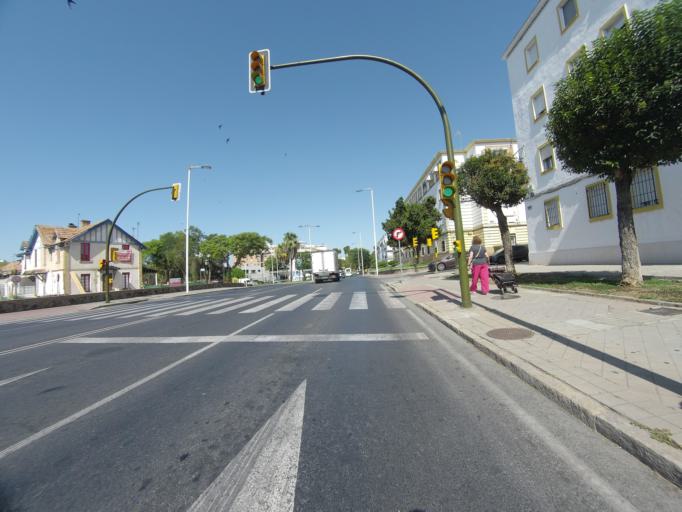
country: ES
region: Andalusia
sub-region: Provincia de Huelva
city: Huelva
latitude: 37.2565
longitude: -6.9401
